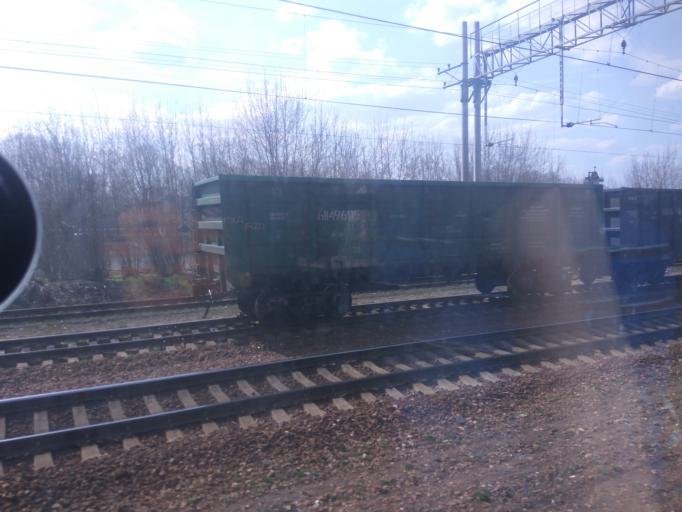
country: RU
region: Moskovskaya
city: Yakhroma
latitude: 56.2848
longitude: 37.5031
